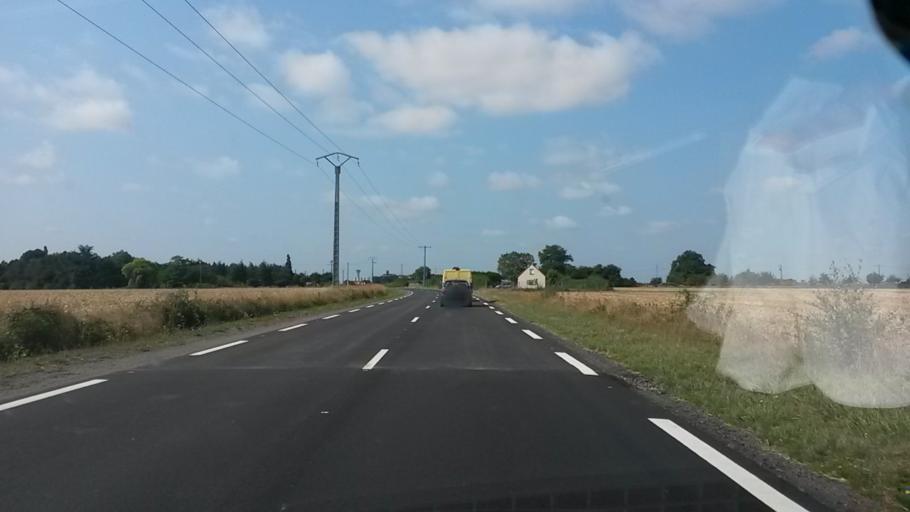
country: FR
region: Haute-Normandie
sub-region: Departement de l'Eure
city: Verneuil-sur-Avre
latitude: 48.7800
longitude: 0.9753
